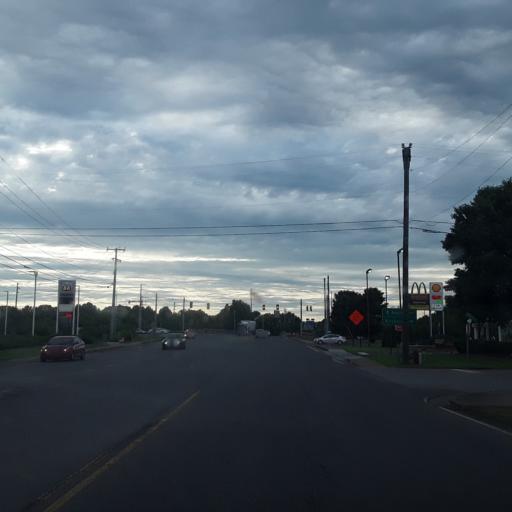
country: US
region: Tennessee
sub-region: Wilson County
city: Green Hill
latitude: 36.1682
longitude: -86.6000
